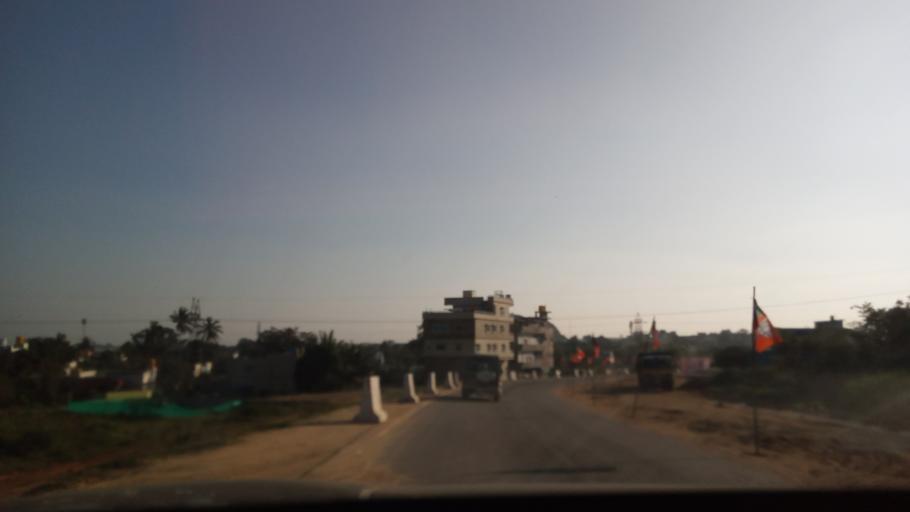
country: IN
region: Tamil Nadu
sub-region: Krishnagiri
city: Hosur
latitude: 12.7244
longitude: 77.8403
